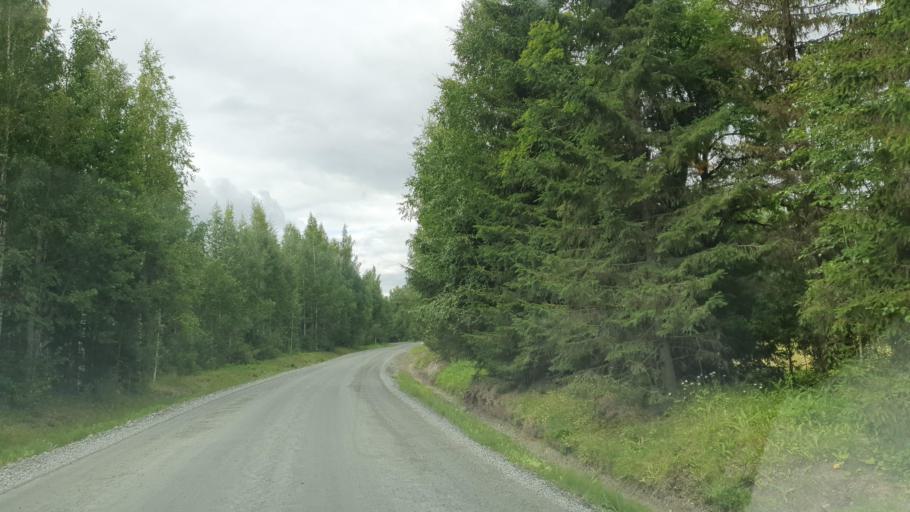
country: FI
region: Northern Savo
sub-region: Ylae-Savo
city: Iisalmi
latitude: 63.5292
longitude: 27.0885
